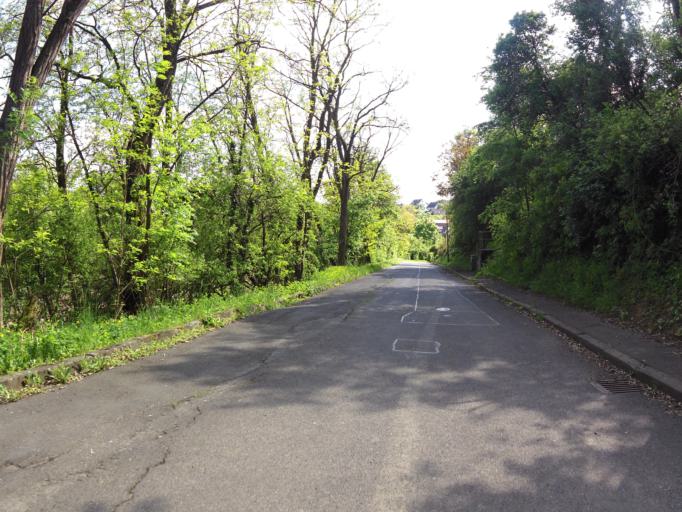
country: DE
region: Bavaria
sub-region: Regierungsbezirk Unterfranken
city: Reichenberg
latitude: 49.7336
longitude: 9.9143
